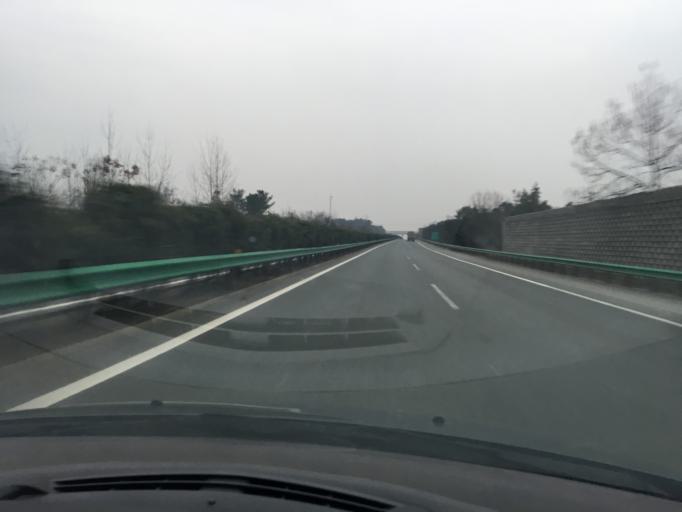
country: CN
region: Hubei
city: Yongjiahe
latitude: 31.0906
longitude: 114.7122
